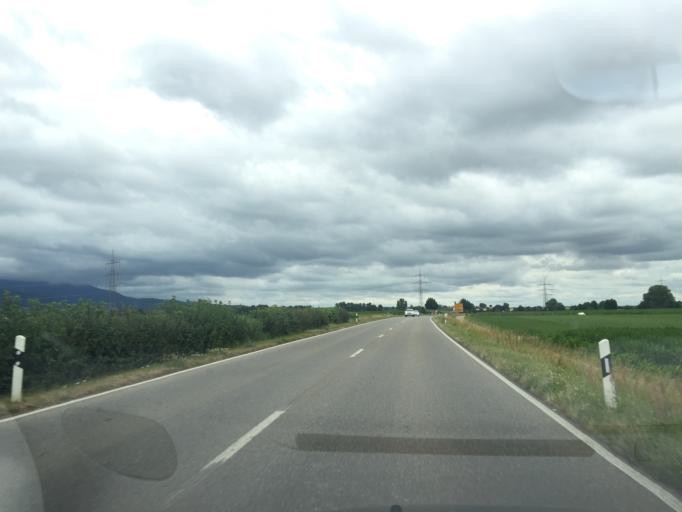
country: DE
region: Baden-Wuerttemberg
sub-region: Freiburg Region
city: Eschbach
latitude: 47.8919
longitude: 7.6713
